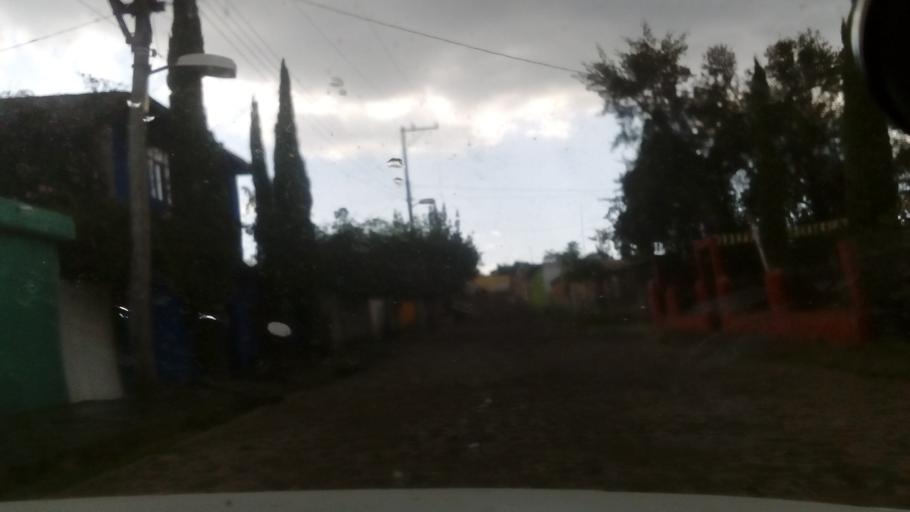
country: MX
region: Guanajuato
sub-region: Silao de la Victoria
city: San Francisco (Banos de Agua Caliente)
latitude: 21.1683
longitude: -101.4160
